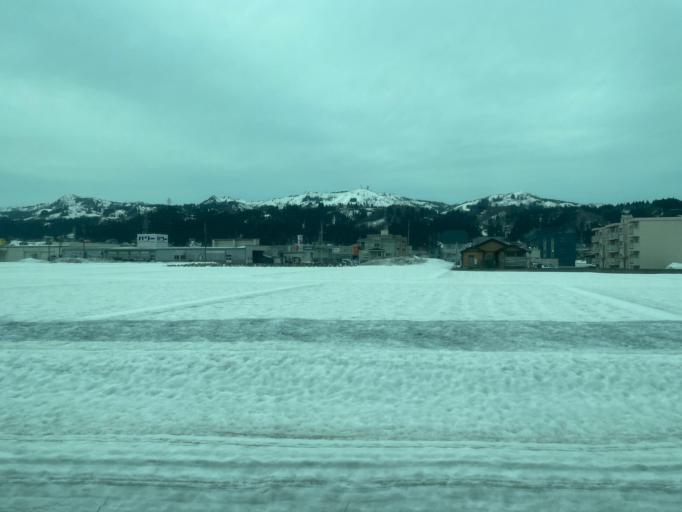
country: JP
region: Niigata
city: Muikamachi
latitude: 37.0604
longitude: 138.8716
